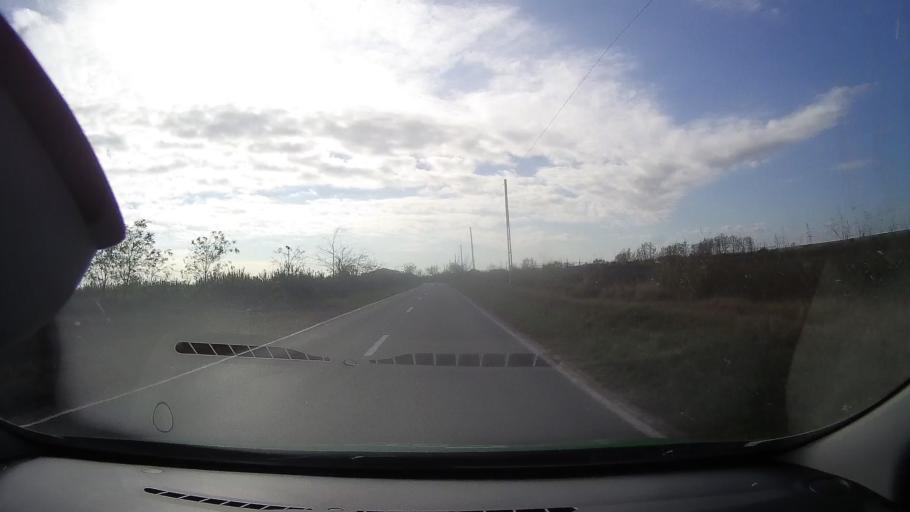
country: RO
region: Tulcea
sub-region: Comuna Sarichioi
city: Sarichioi
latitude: 44.9823
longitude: 28.8835
